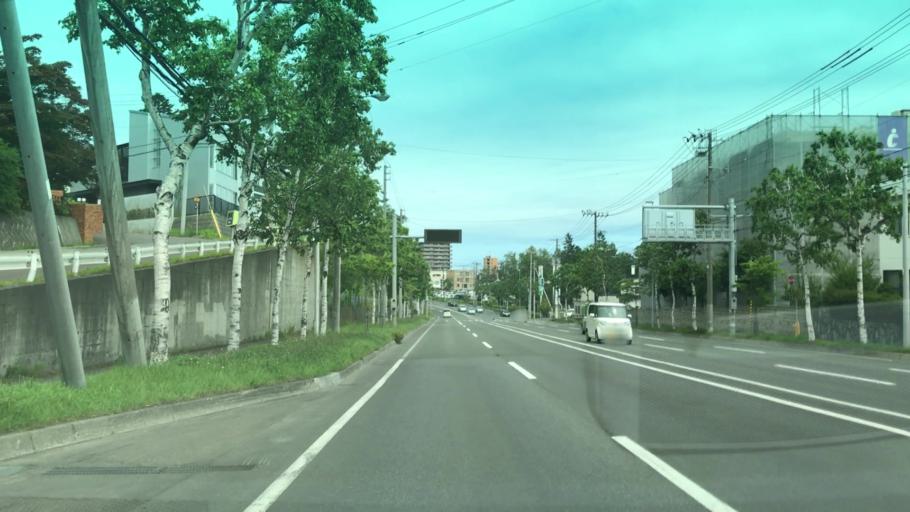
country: JP
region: Hokkaido
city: Sapporo
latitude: 43.0677
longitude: 141.2881
